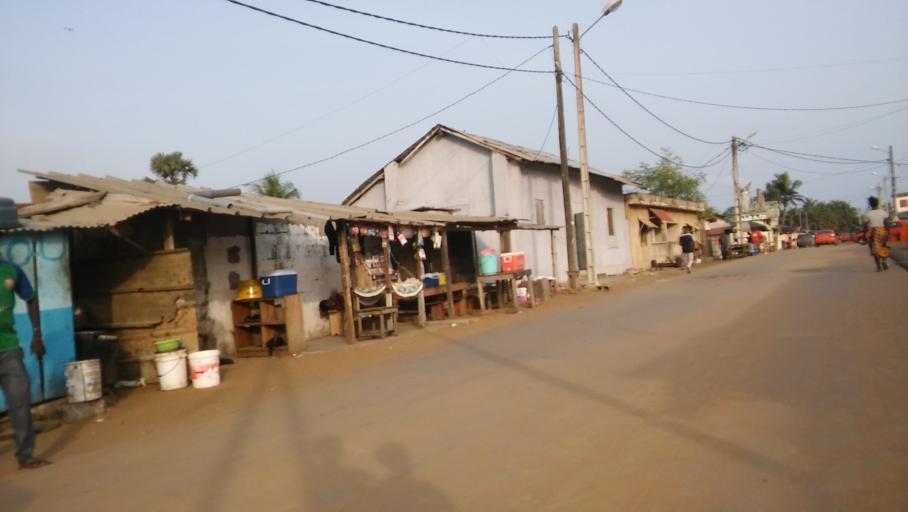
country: CI
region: Sud-Comoe
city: Grand-Bassam
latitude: 5.1949
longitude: -3.7273
